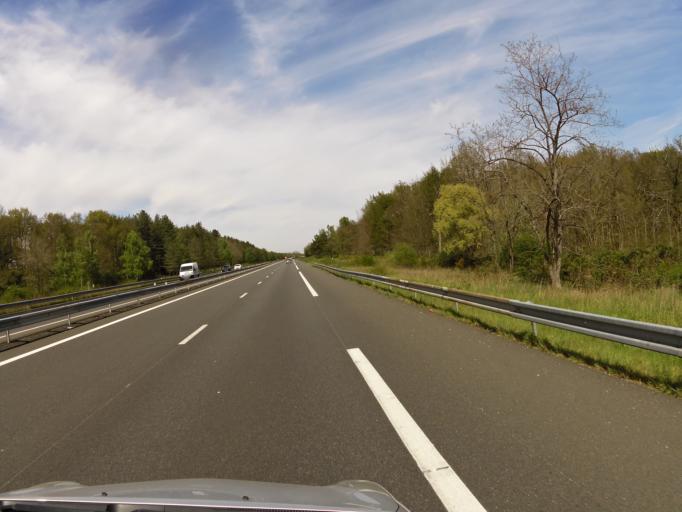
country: FR
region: Centre
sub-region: Departement du Loiret
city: Jouy-le-Potier
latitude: 47.7900
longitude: 1.8471
